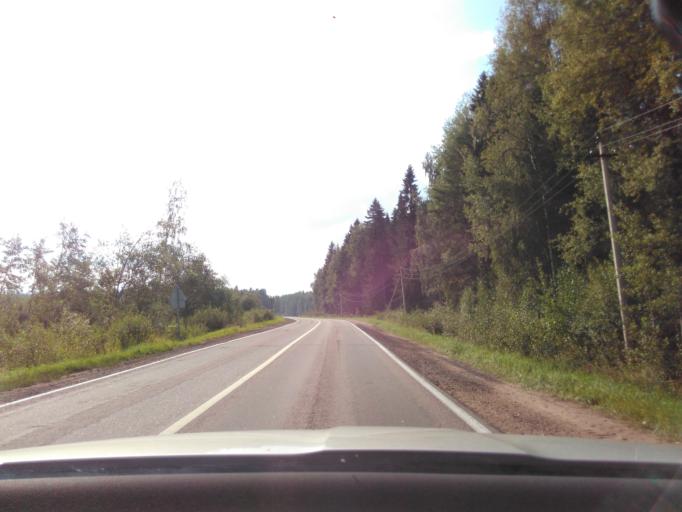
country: RU
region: Moskovskaya
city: Solnechnogorsk
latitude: 56.1457
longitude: 36.8268
